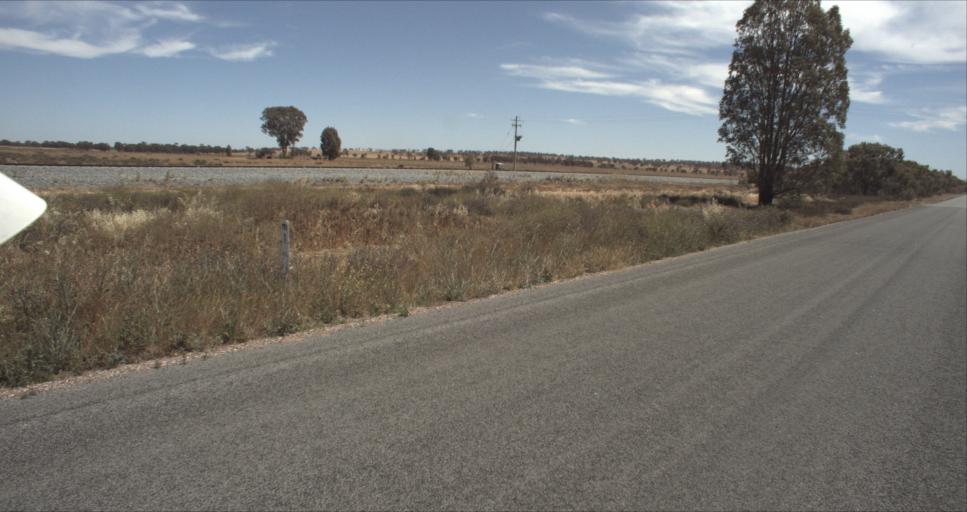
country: AU
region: New South Wales
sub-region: Leeton
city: Leeton
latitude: -34.6350
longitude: 146.4605
